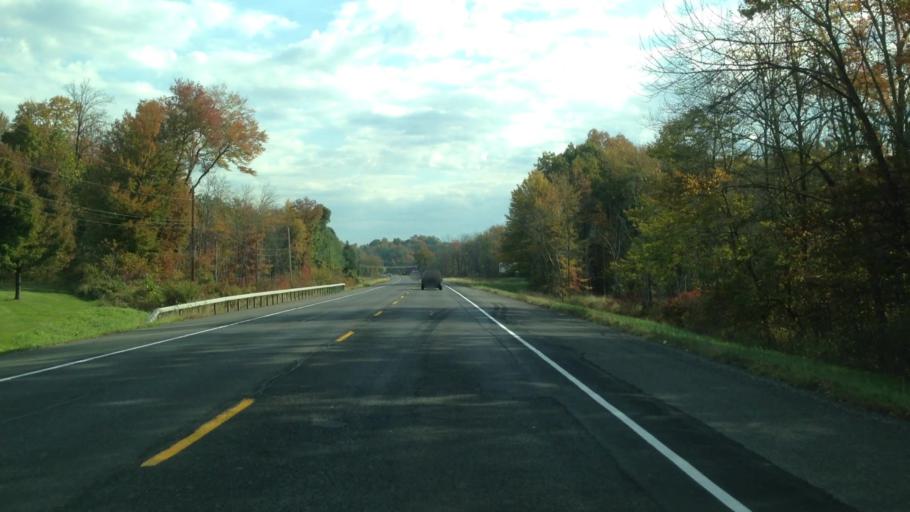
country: US
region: New York
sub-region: Ulster County
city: Clintondale
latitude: 41.7375
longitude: -74.0230
